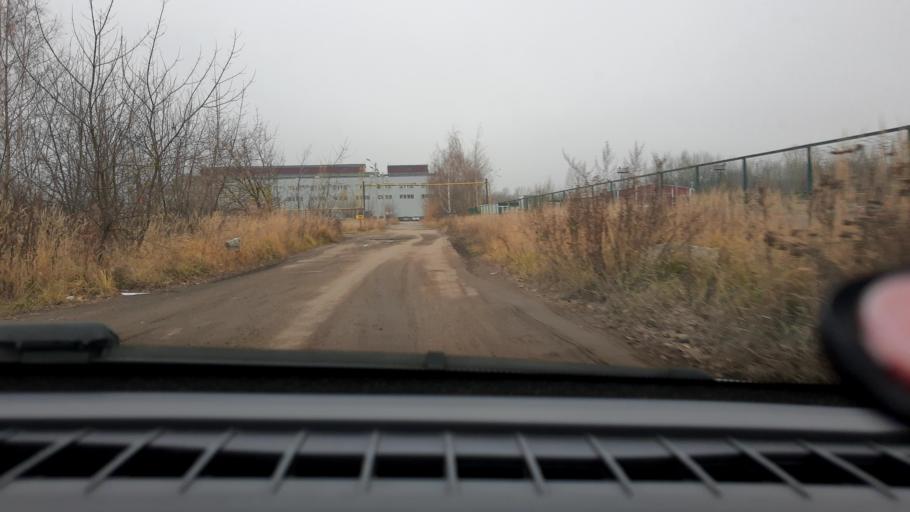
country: RU
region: Nizjnij Novgorod
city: Nizhniy Novgorod
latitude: 56.3337
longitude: 43.9000
